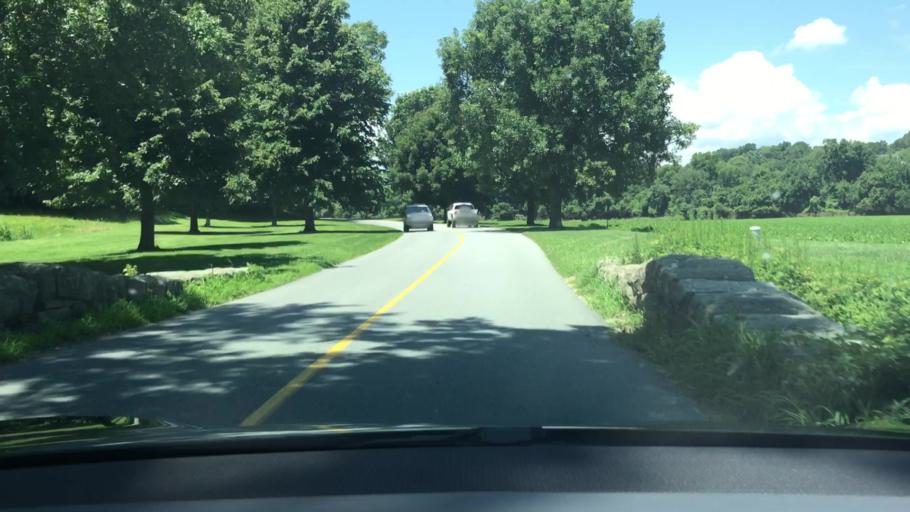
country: US
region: North Carolina
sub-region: Buncombe County
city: Asheville
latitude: 35.5644
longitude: -82.5657
